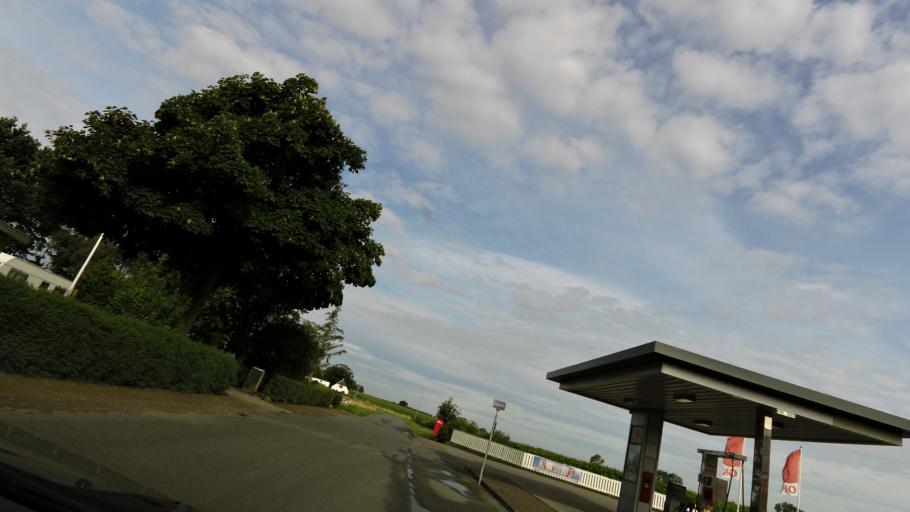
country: DK
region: South Denmark
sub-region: Nordfyns Kommune
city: Otterup
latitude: 55.5744
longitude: 10.3935
